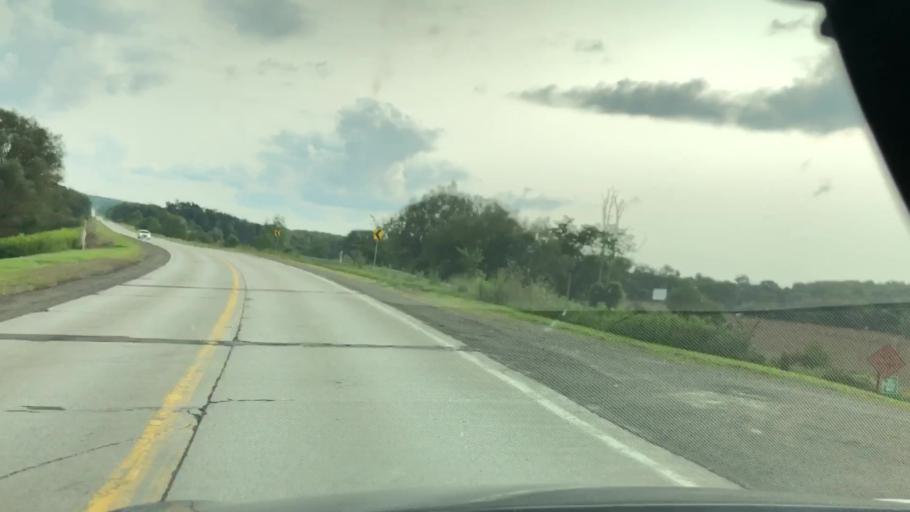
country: US
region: Pennsylvania
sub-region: Erie County
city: Union City
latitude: 41.9834
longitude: -79.8369
